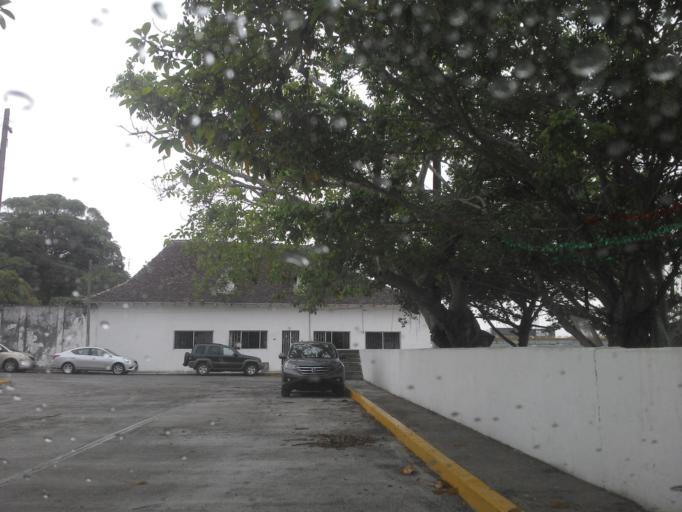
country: MX
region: Veracruz
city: Nautla
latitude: 20.2128
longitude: -96.7785
